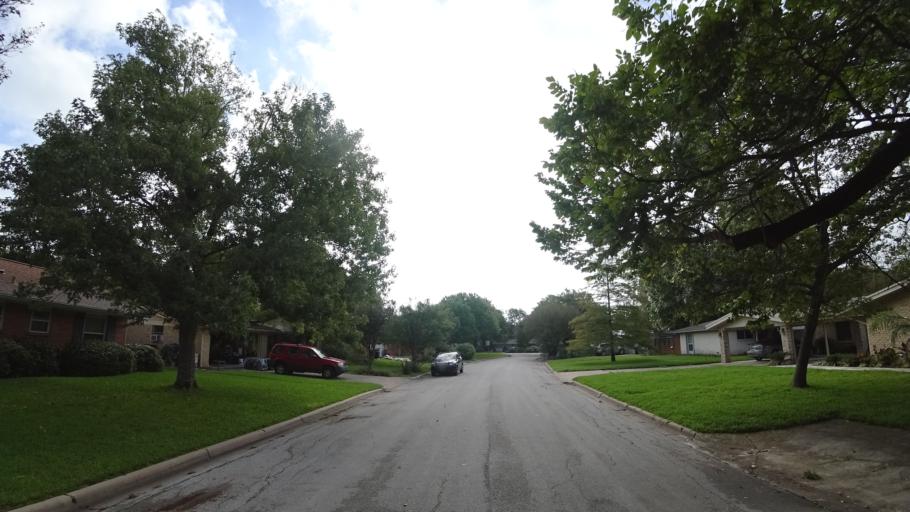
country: US
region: Texas
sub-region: Travis County
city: West Lake Hills
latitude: 30.3533
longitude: -97.7421
